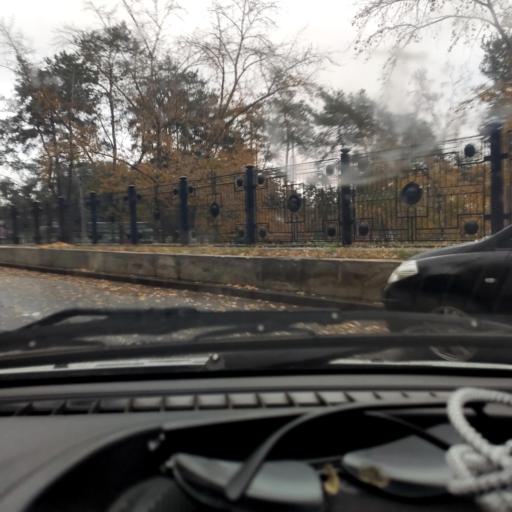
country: RU
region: Samara
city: Zhigulevsk
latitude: 53.4803
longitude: 49.4636
